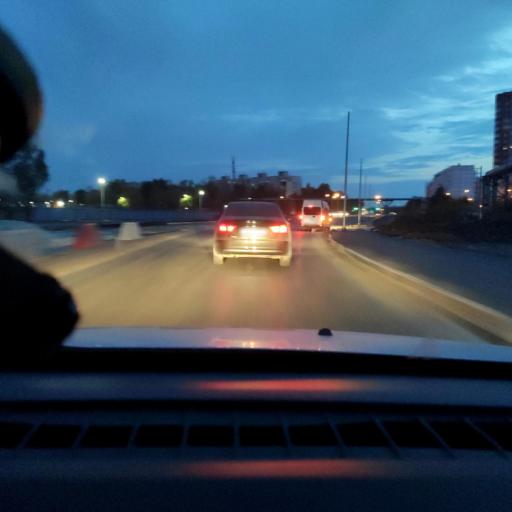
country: RU
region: Samara
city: Samara
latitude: 53.1048
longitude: 50.0787
